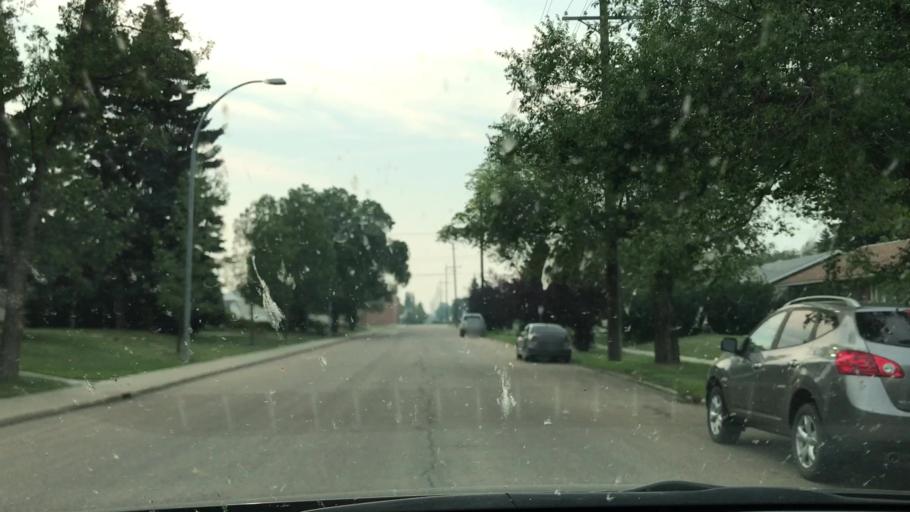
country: CA
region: Alberta
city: Edmonton
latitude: 53.5923
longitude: -113.5513
